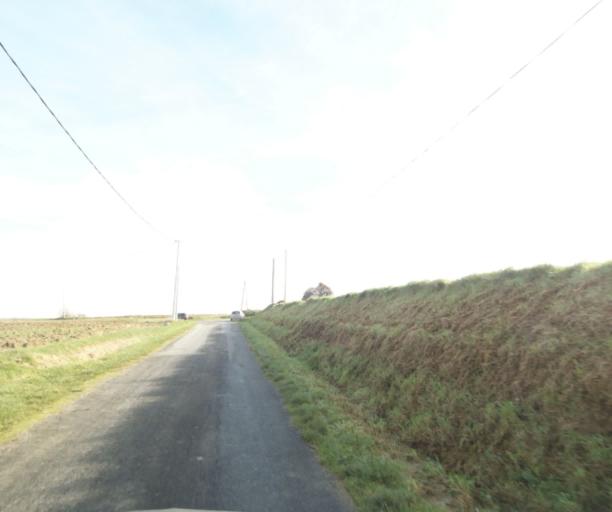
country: FR
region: Midi-Pyrenees
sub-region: Departement de la Haute-Garonne
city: Villemur-sur-Tarn
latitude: 43.8533
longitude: 1.5224
